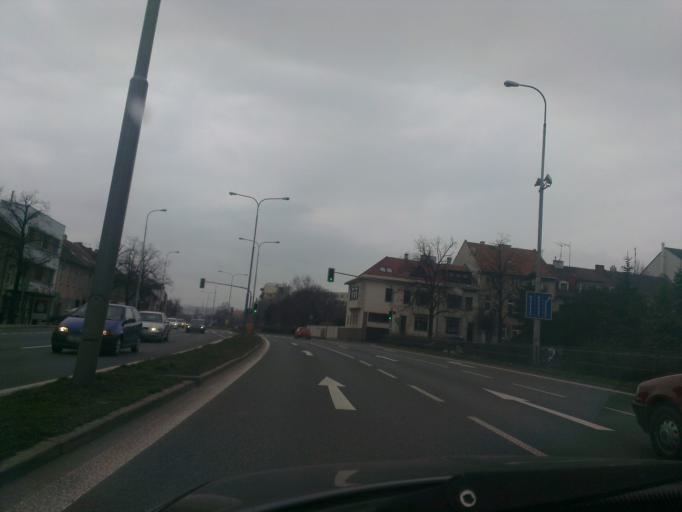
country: CZ
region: South Moravian
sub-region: Mesto Brno
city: Brno
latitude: 49.1984
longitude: 16.6459
